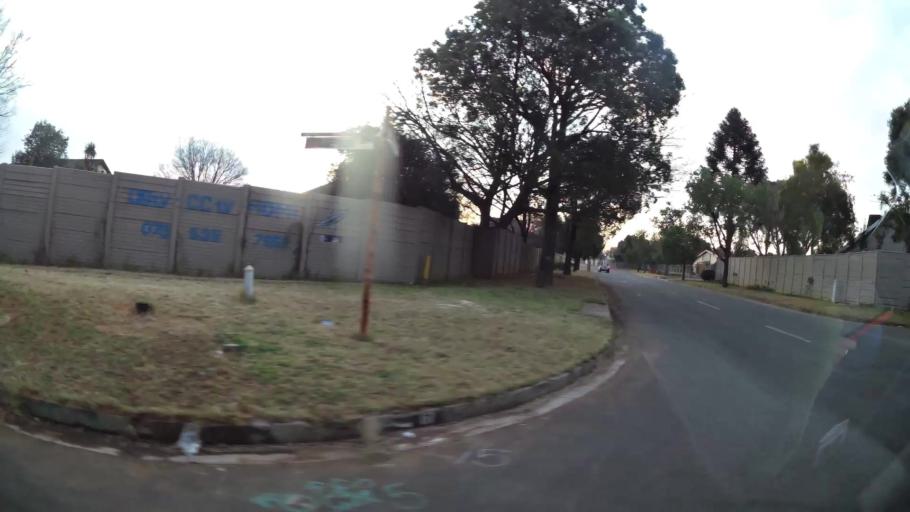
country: ZA
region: Gauteng
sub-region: Ekurhuleni Metropolitan Municipality
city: Benoni
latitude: -26.1729
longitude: 28.2974
